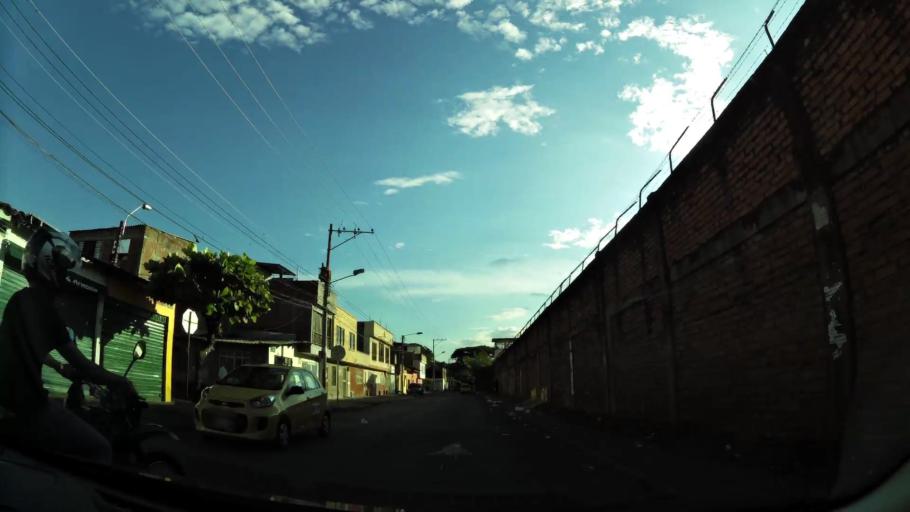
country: CO
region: Valle del Cauca
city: Cali
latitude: 3.4315
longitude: -76.5100
